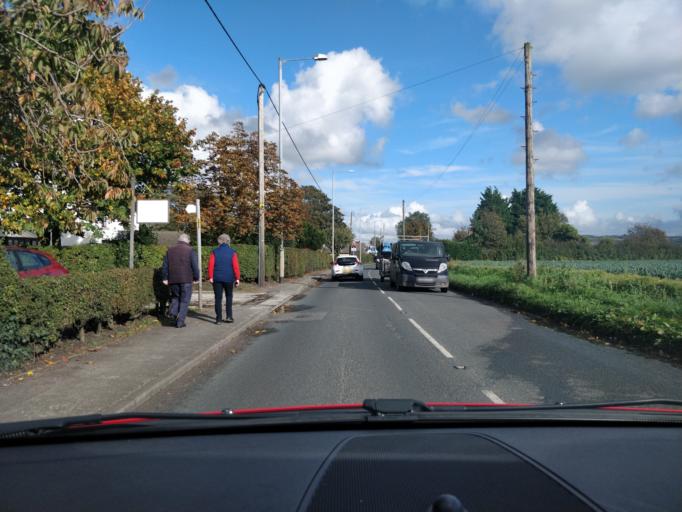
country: GB
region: England
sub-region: Lancashire
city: Parbold
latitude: 53.5970
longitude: -2.8076
